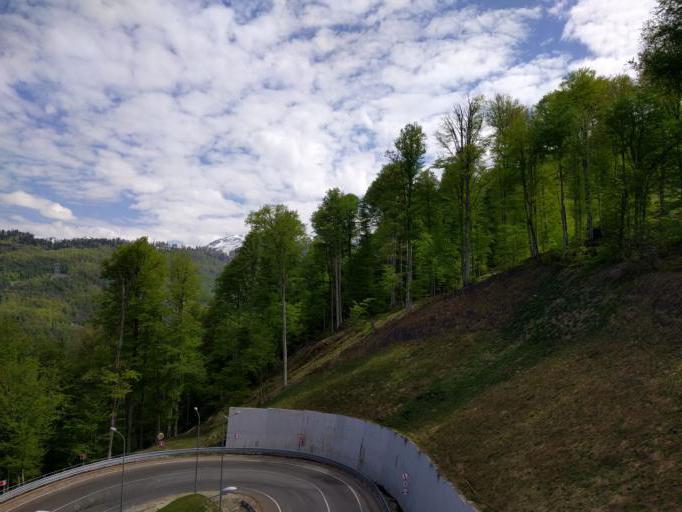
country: RU
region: Krasnodarskiy
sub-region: Sochi City
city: Krasnaya Polyana
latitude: 43.6642
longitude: 40.3101
